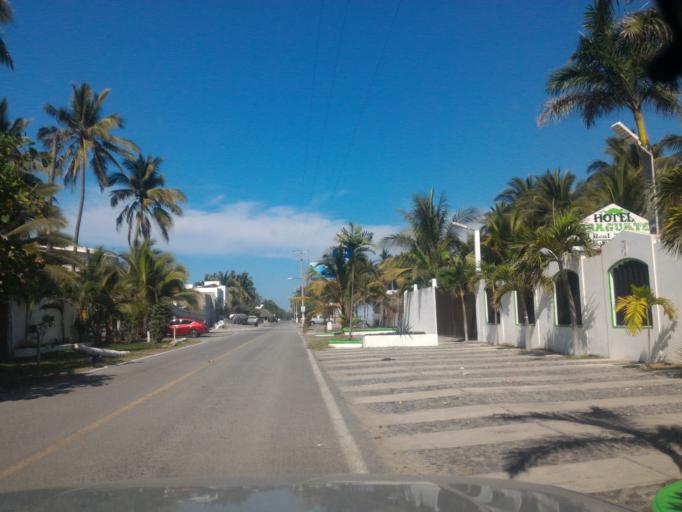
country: MX
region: Colima
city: Armeria
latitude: 18.8416
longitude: -103.9451
